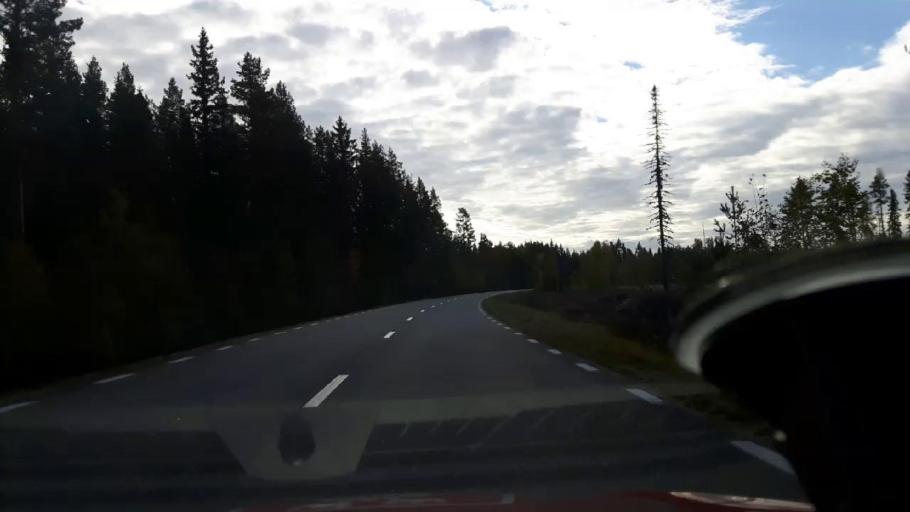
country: SE
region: Gaevleborg
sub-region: Ljusdals Kommun
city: Farila
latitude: 62.0174
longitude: 15.2371
